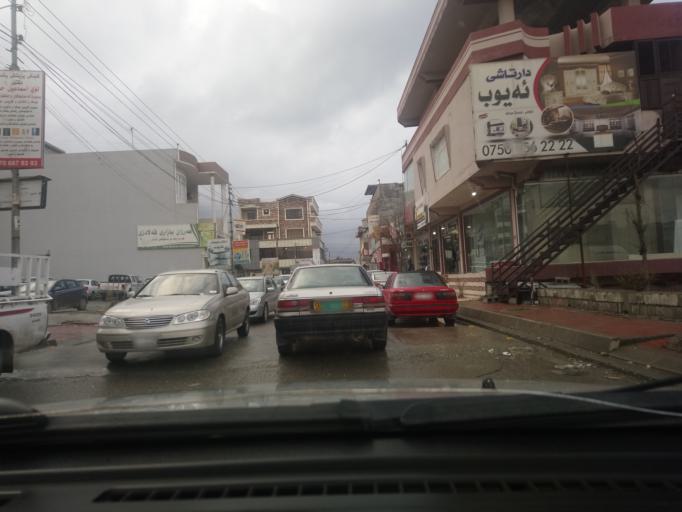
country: IQ
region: As Sulaymaniyah
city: Qeladize
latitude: 36.1848
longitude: 45.1283
